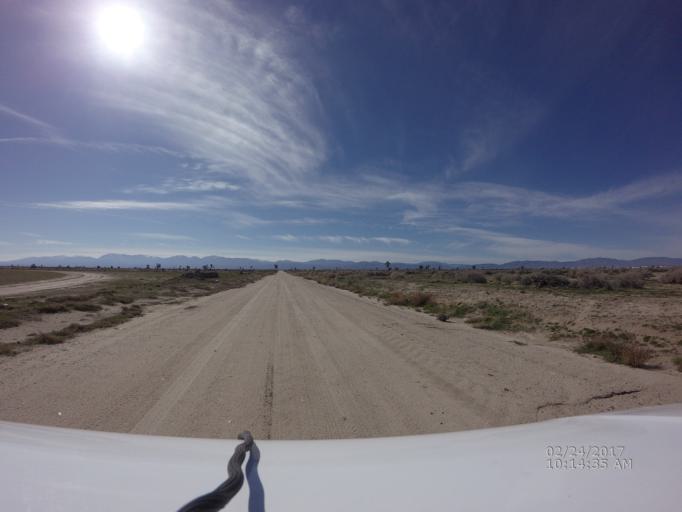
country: US
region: California
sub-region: Los Angeles County
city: Littlerock
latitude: 34.6622
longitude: -117.9874
